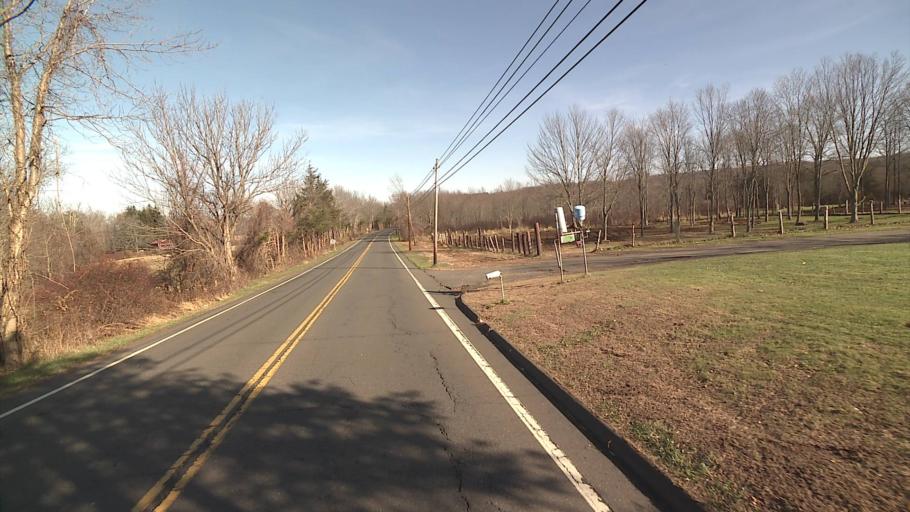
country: US
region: Connecticut
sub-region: Middlesex County
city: Durham
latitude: 41.4573
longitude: -72.6929
